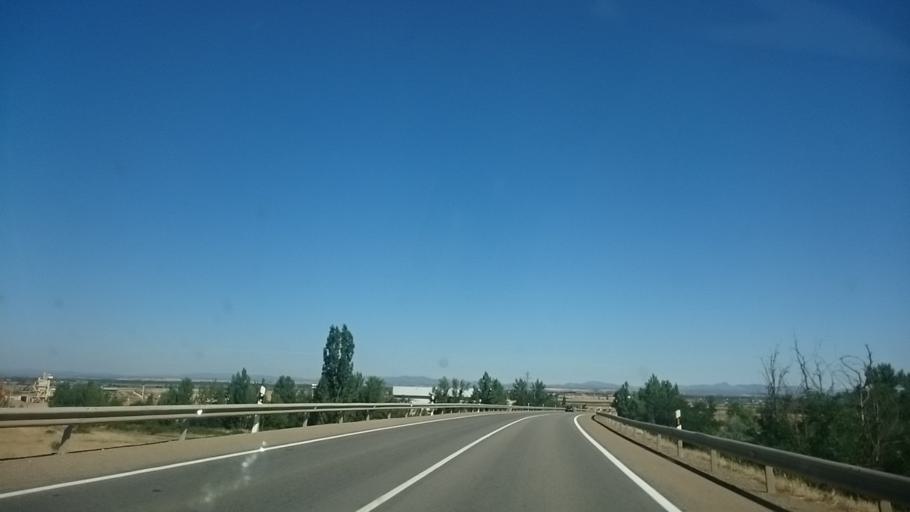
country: ES
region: Castille and Leon
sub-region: Provincia de Leon
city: Santas Martas
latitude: 42.4606
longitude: -5.3912
